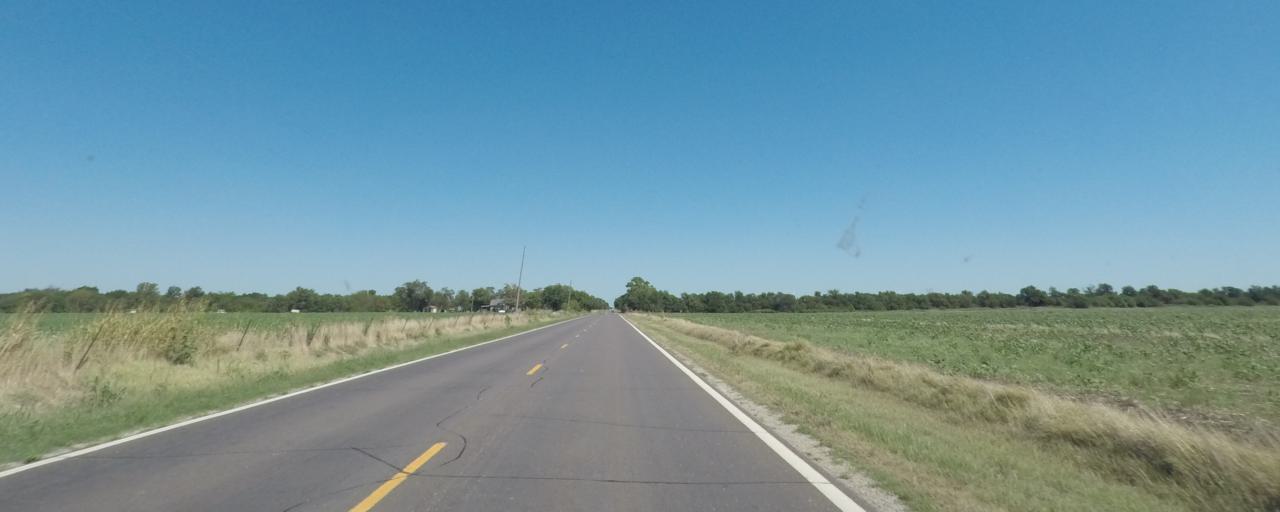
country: US
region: Kansas
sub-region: Sumner County
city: Wellington
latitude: 37.1007
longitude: -97.4015
